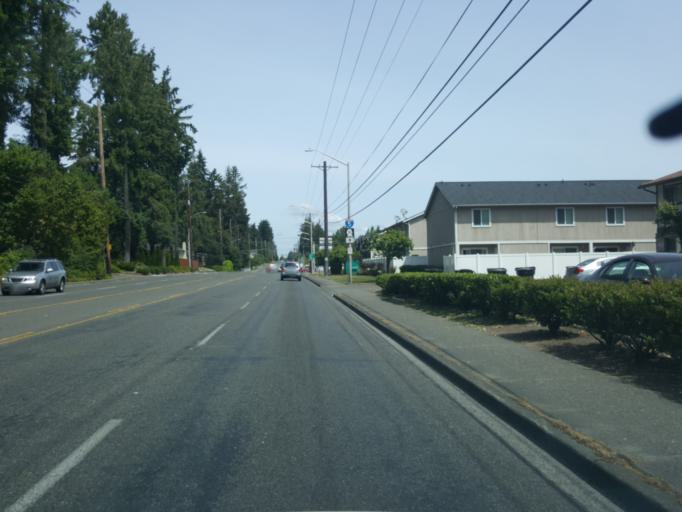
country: US
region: Washington
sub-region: Pierce County
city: Fircrest
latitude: 47.2318
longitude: -122.5050
